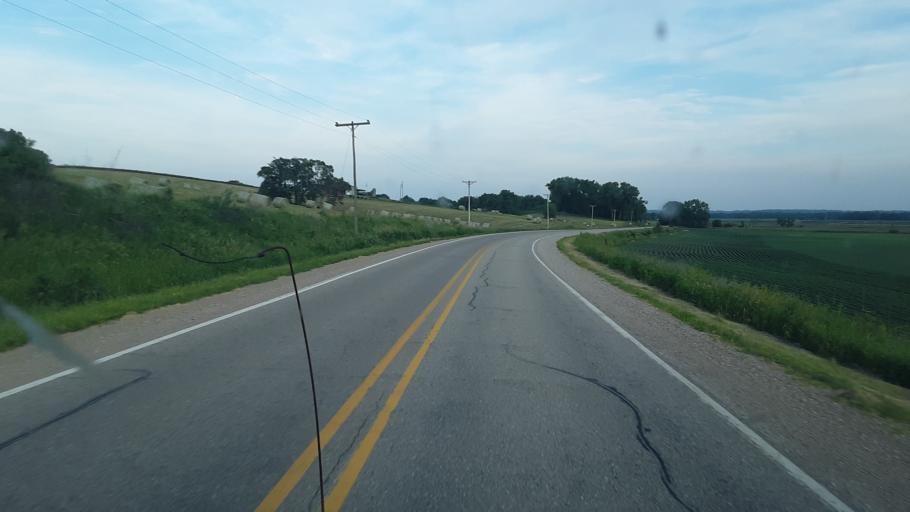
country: US
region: Iowa
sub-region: Tama County
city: Tama
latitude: 41.9557
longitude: -92.4242
